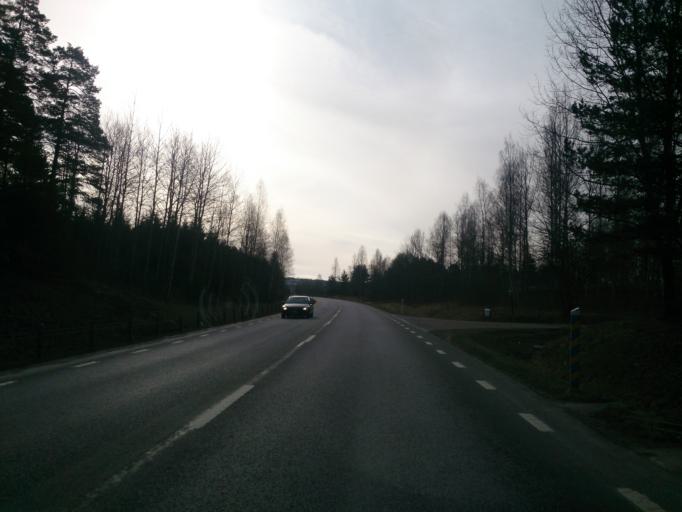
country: SE
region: OEstergoetland
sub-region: Atvidabergs Kommun
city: Atvidaberg
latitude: 58.2390
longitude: 15.9393
